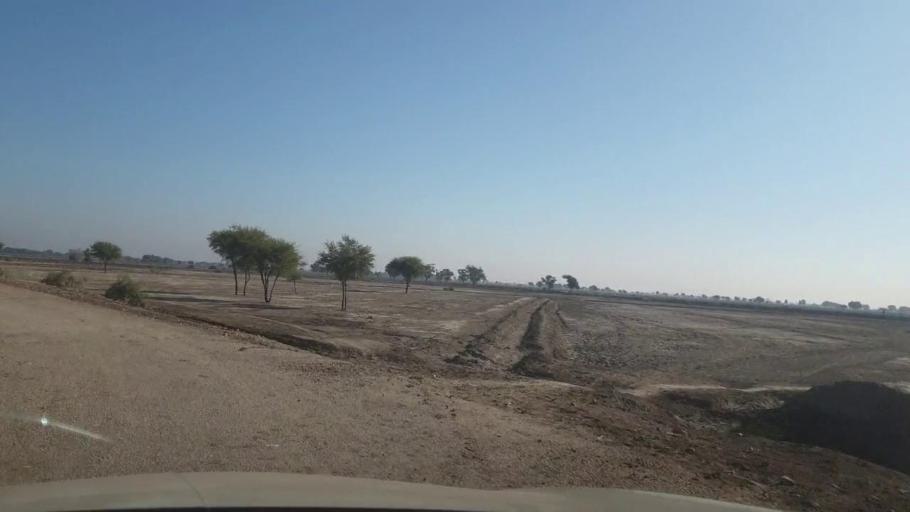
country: PK
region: Sindh
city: Bhan
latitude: 26.5201
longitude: 67.6741
